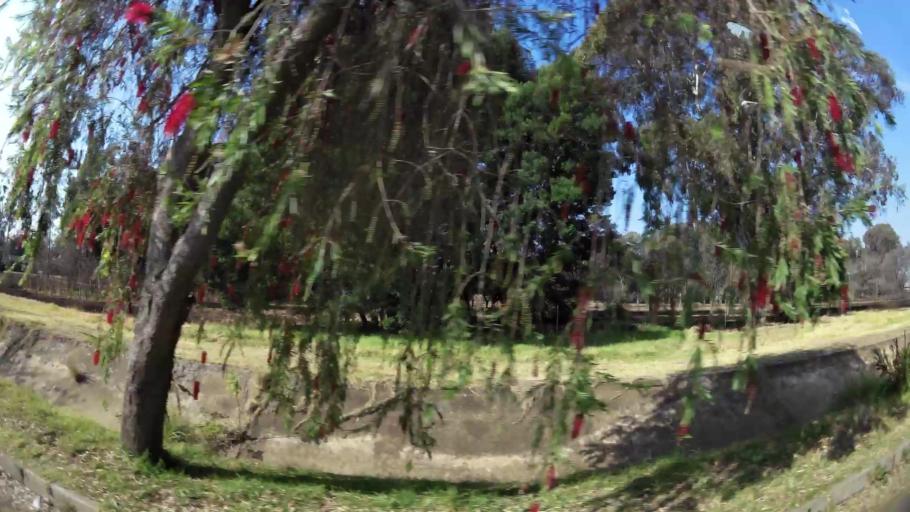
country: ZA
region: Gauteng
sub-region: West Rand District Municipality
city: Randfontein
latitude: -26.1685
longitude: 27.6890
